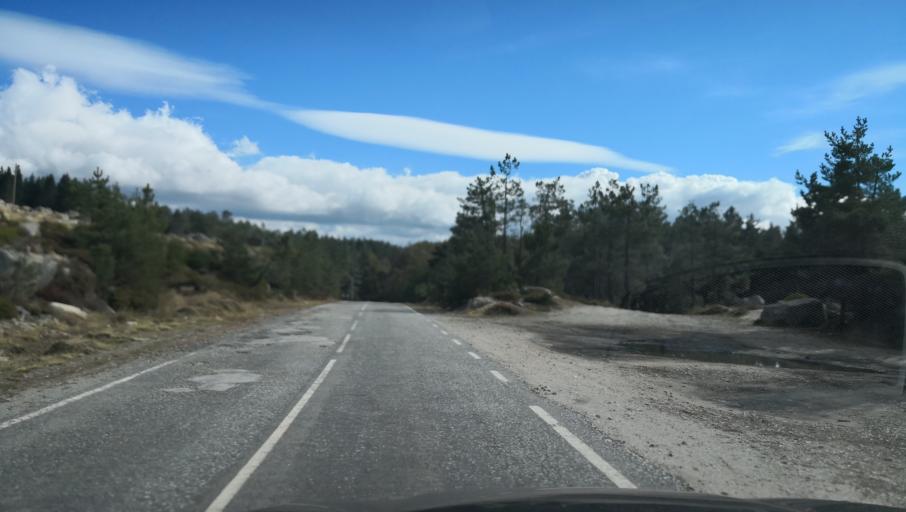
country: PT
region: Vila Real
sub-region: Vila Real
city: Vila Real
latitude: 41.3505
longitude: -7.7926
